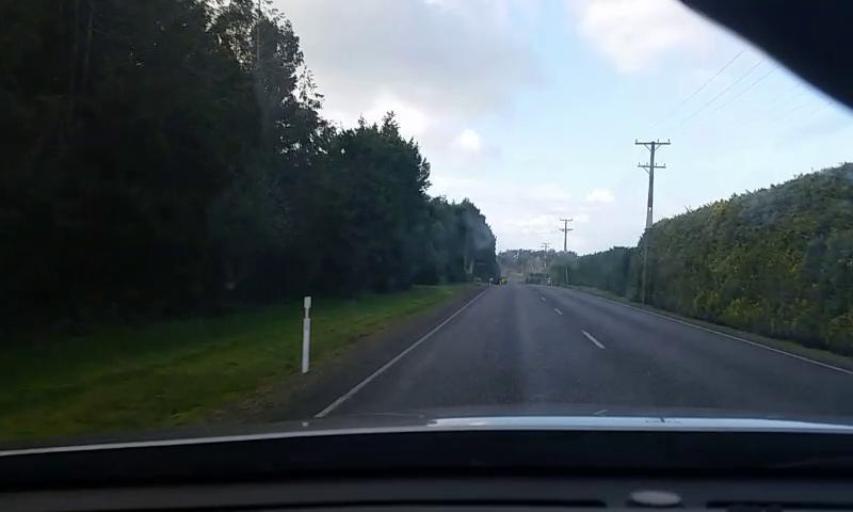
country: NZ
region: Southland
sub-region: Invercargill City
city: Invercargill
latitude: -46.3806
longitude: 168.4307
